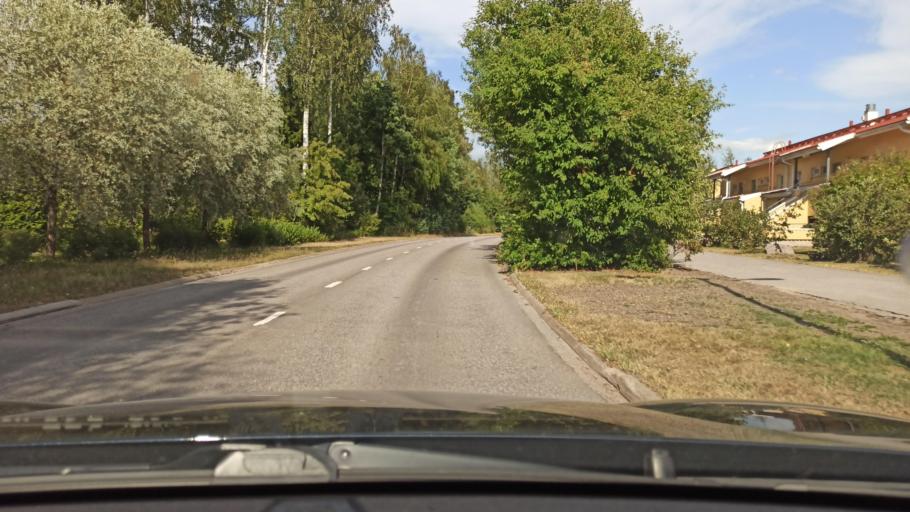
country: FI
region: Uusimaa
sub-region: Helsinki
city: Kirkkonummi
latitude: 60.1276
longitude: 24.4165
